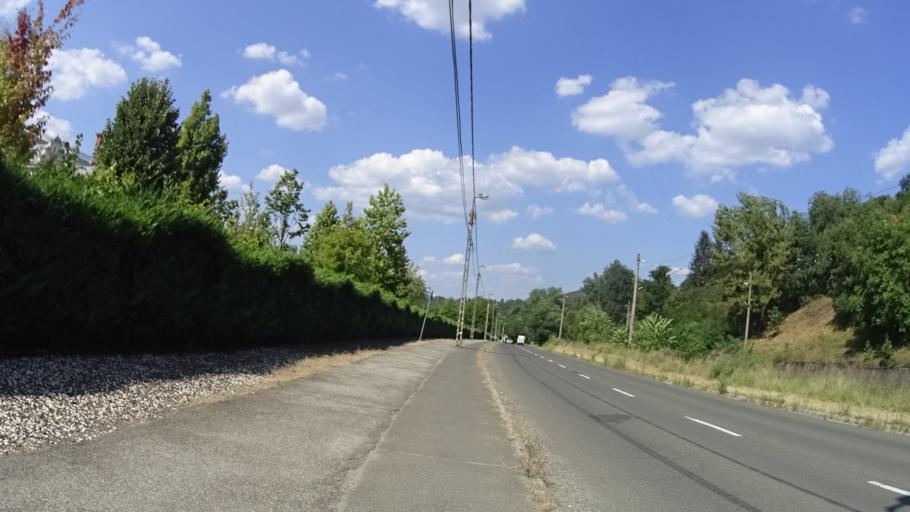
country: HU
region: Komarom-Esztergom
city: Pilismarot
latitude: 47.7908
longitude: 18.9099
